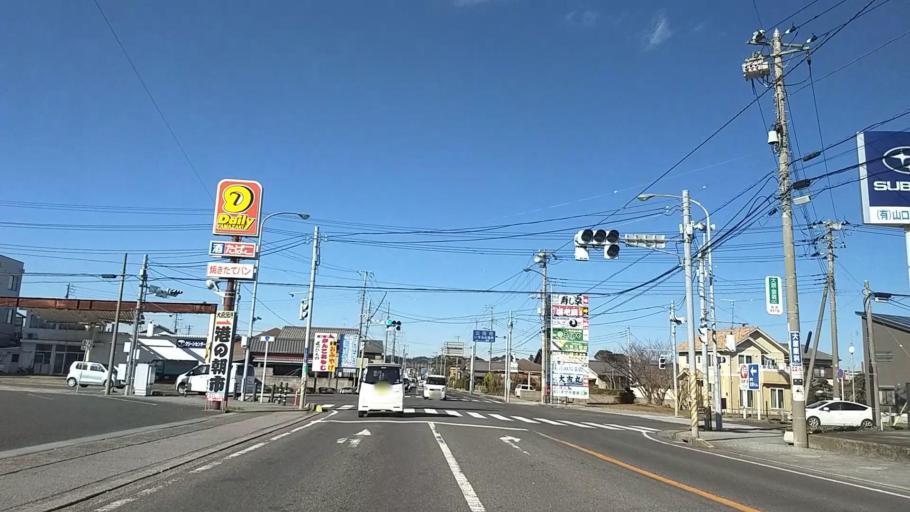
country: JP
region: Chiba
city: Ohara
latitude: 35.2536
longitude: 140.3955
